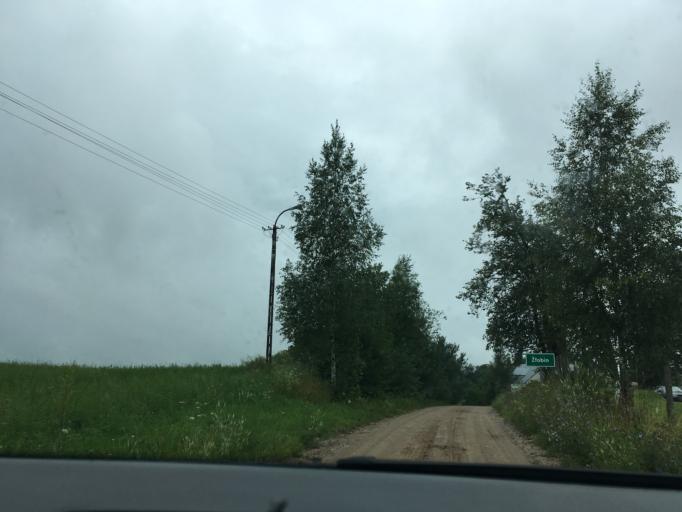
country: PL
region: Podlasie
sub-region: Powiat sejnenski
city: Krasnopol
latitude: 54.0929
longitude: 23.2683
